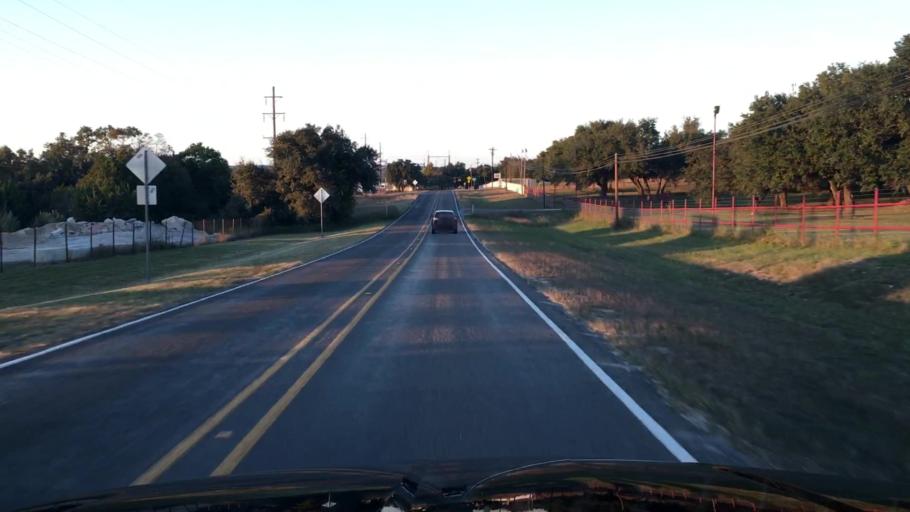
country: US
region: Texas
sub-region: Blanco County
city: Blanco
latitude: 30.0783
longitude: -98.4121
